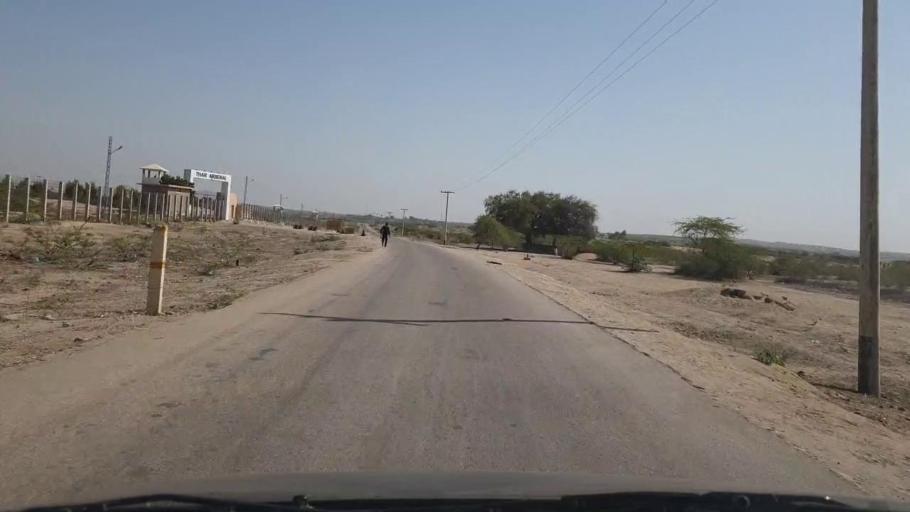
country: PK
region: Sindh
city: Chor
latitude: 25.5154
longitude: 69.8087
